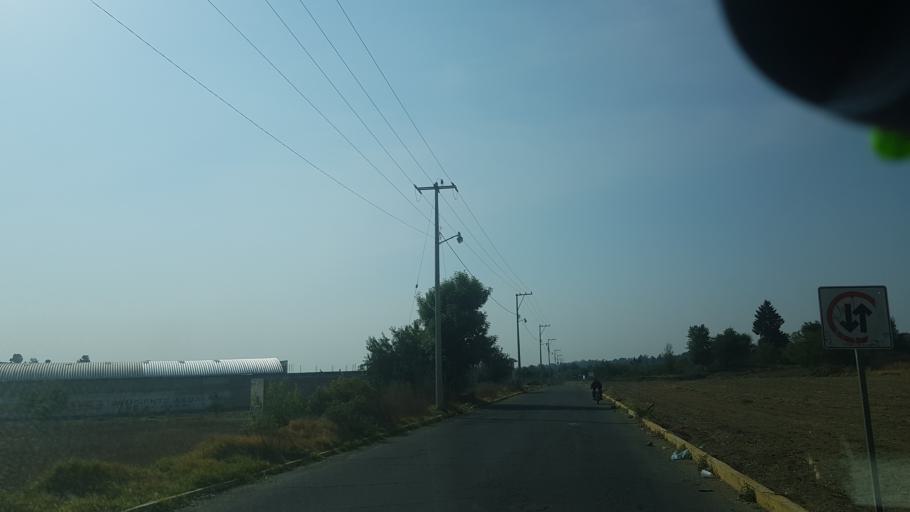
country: MX
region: Puebla
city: San Nicolas de los Ranchos
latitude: 19.0660
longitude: -98.4734
